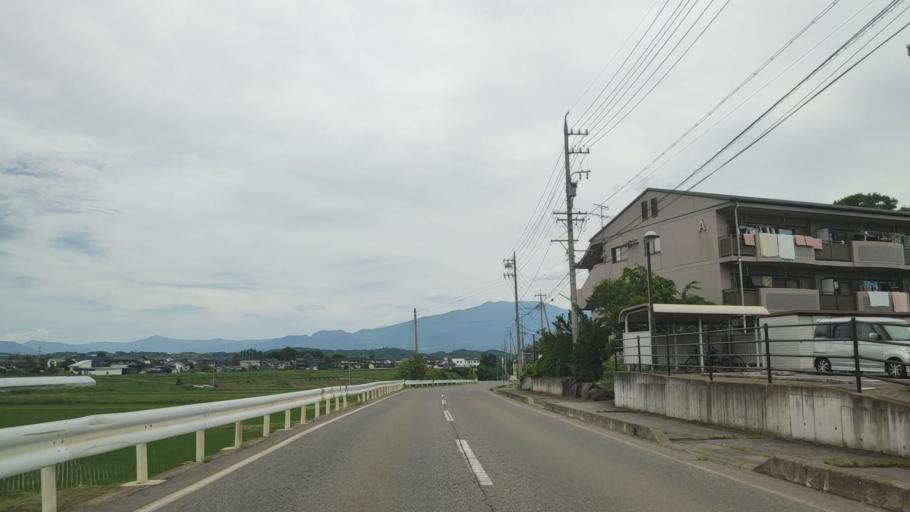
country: JP
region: Nagano
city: Kamimaruko
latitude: 36.2943
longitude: 138.3173
